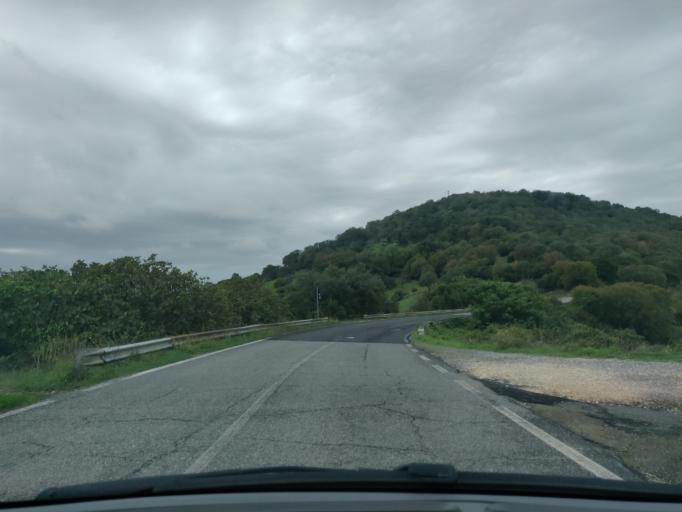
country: IT
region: Latium
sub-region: Citta metropolitana di Roma Capitale
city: Allumiere
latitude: 42.1439
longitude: 11.8794
